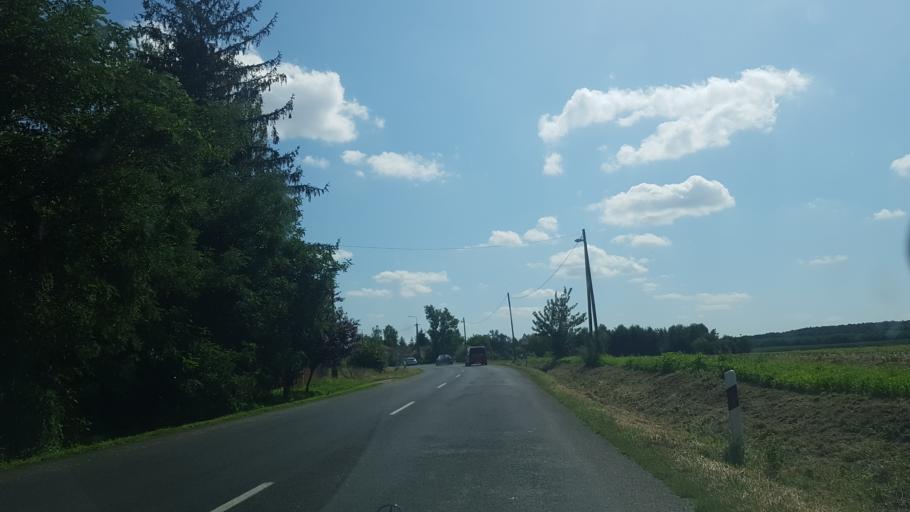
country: HU
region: Somogy
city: Marcali
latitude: 46.5320
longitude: 17.4172
